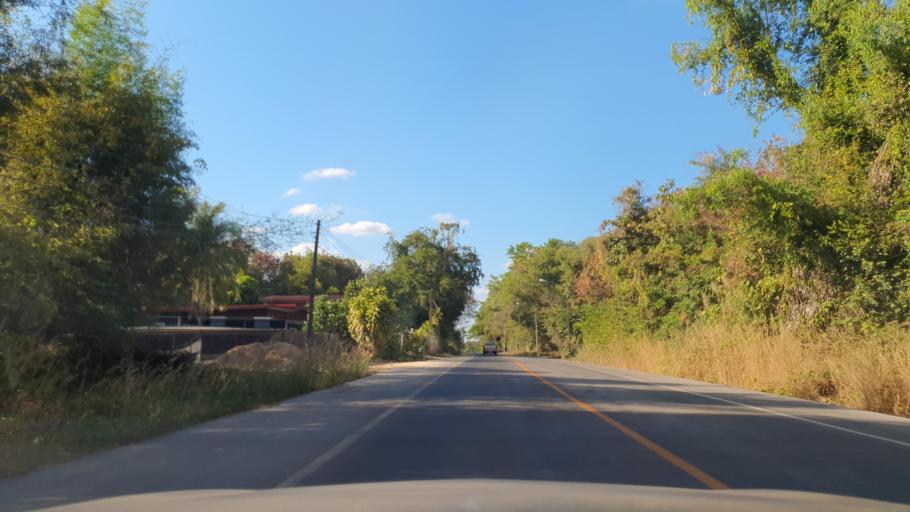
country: TH
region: Nong Khai
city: Bueng Khong Long
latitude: 18.0051
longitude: 104.0116
